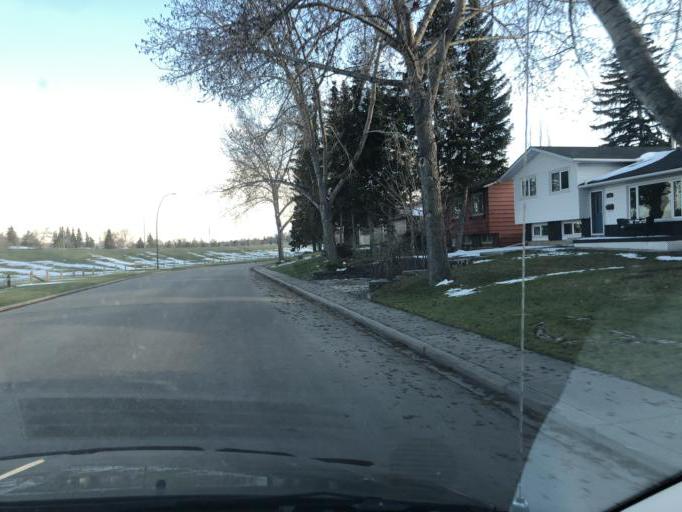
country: CA
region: Alberta
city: Calgary
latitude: 50.9389
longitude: -114.0331
